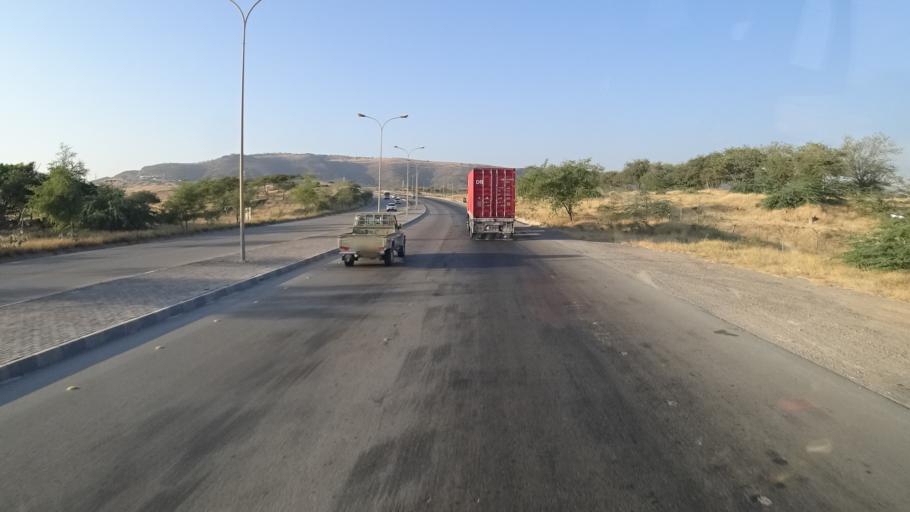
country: OM
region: Zufar
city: Salalah
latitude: 17.1154
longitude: 54.1530
